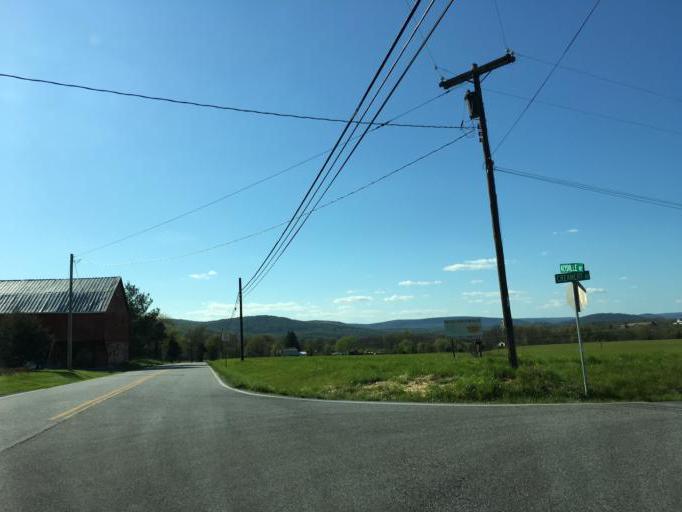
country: US
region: Maryland
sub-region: Frederick County
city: Emmitsburg
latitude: 39.6835
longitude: -77.3212
